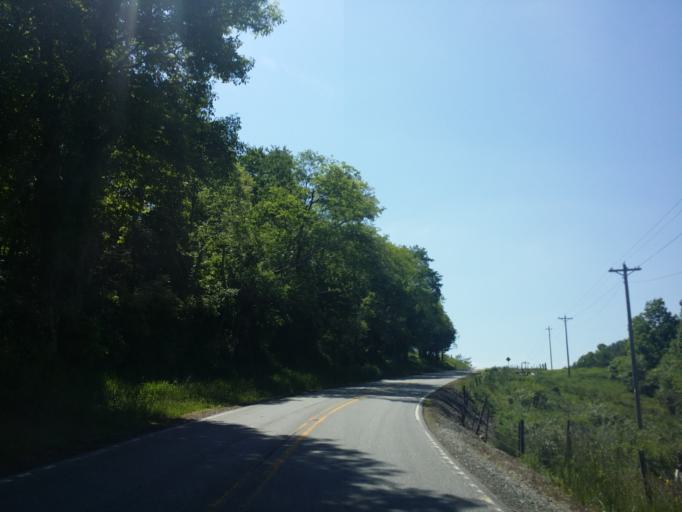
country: US
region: North Carolina
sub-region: Madison County
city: Marshall
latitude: 35.7137
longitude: -82.8350
